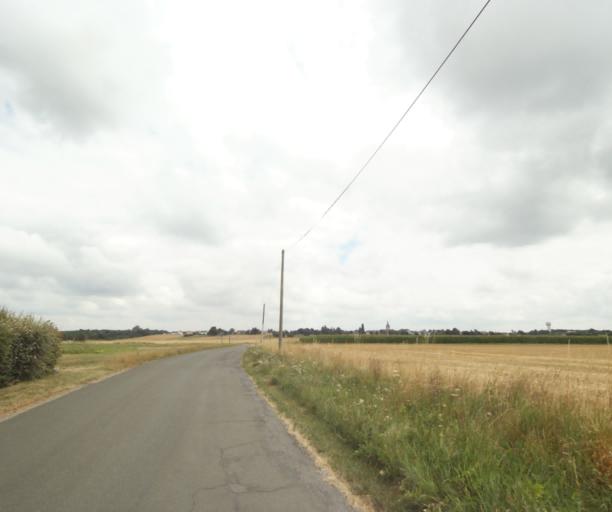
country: FR
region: Centre
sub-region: Departement du Loiret
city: Mardie
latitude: 47.8791
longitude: 2.0506
